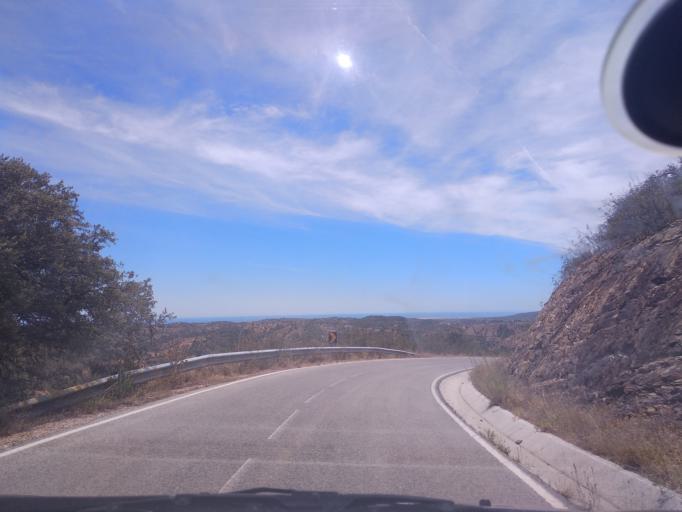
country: PT
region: Faro
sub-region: Sao Bras de Alportel
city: Sao Bras de Alportel
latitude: 37.1902
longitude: -7.7971
